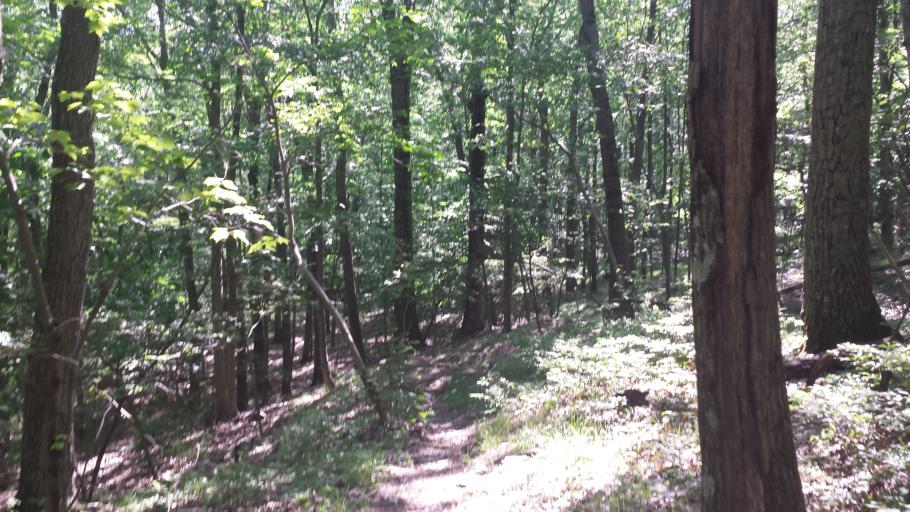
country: US
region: New York
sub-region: Putnam County
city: Peach Lake
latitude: 41.3105
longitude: -73.5534
